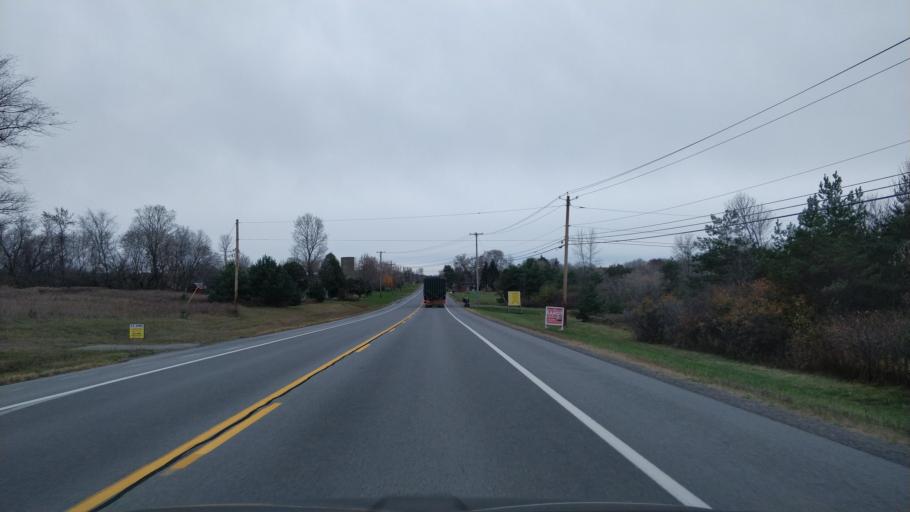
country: CA
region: Ontario
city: Brockville
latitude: 44.6265
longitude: -75.5877
